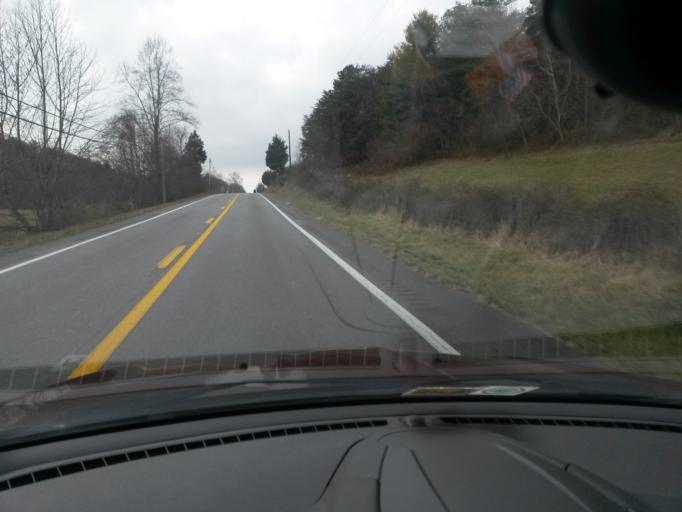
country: US
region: Virginia
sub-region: Alleghany County
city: Clifton Forge
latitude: 37.7420
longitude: -79.7945
